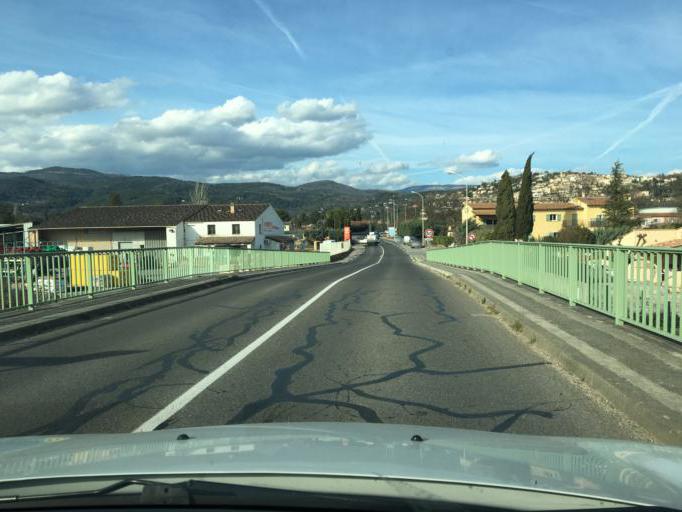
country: FR
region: Provence-Alpes-Cote d'Azur
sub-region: Departement du Var
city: Fayence
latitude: 43.6120
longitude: 6.6870
